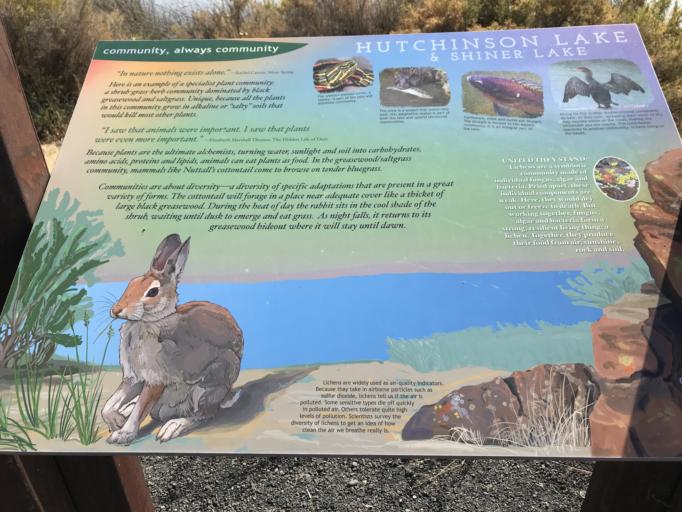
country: US
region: Washington
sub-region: Adams County
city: Othello
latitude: 46.8774
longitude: -119.2973
